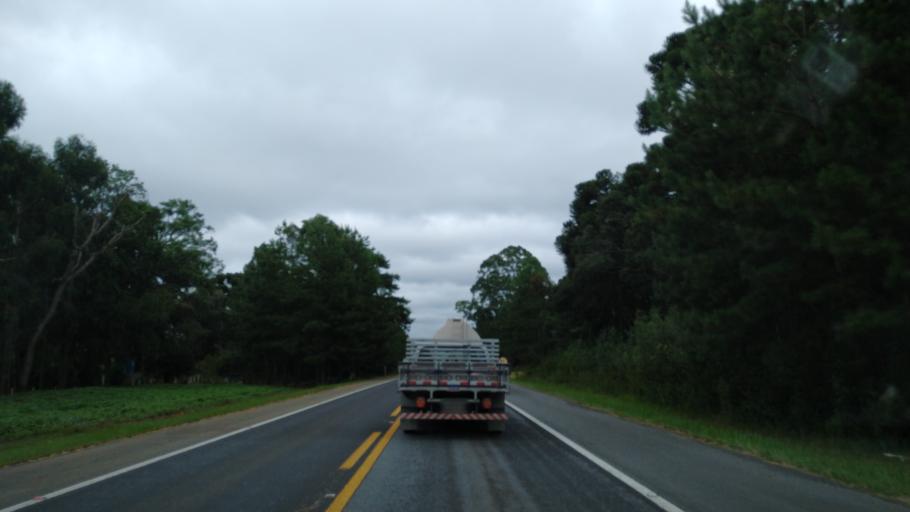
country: BR
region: Santa Catarina
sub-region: Tres Barras
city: Tres Barras
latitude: -26.1729
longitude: -50.0789
